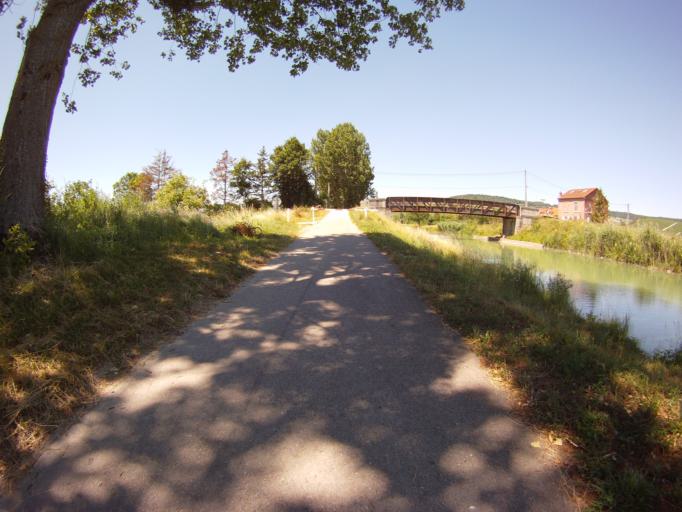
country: FR
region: Champagne-Ardenne
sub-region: Departement de la Marne
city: Dizy
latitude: 49.0667
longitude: 3.9500
